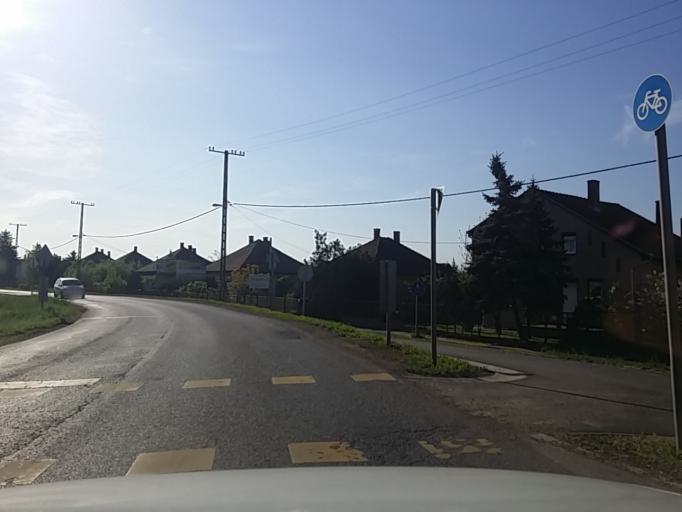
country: HU
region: Jasz-Nagykun-Szolnok
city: Mezotur
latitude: 47.0153
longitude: 20.6104
